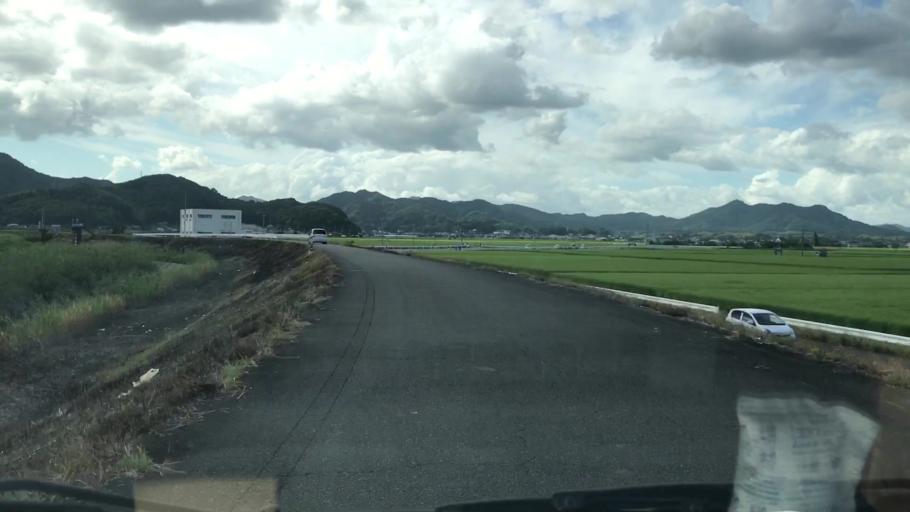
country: JP
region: Saga Prefecture
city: Kashima
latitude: 33.1126
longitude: 130.0836
